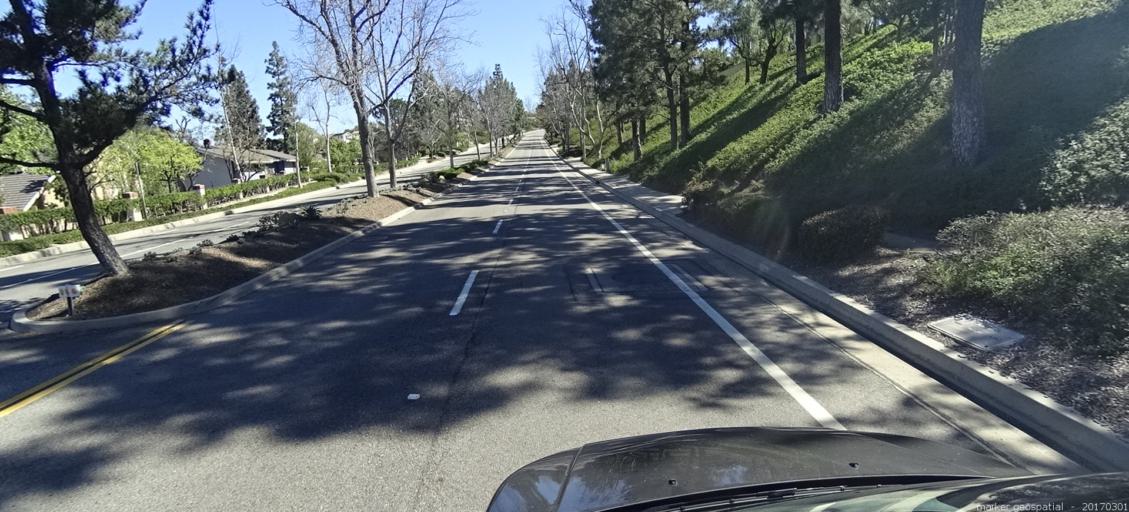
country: US
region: California
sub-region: Orange County
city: Villa Park
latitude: 33.8458
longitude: -117.7531
